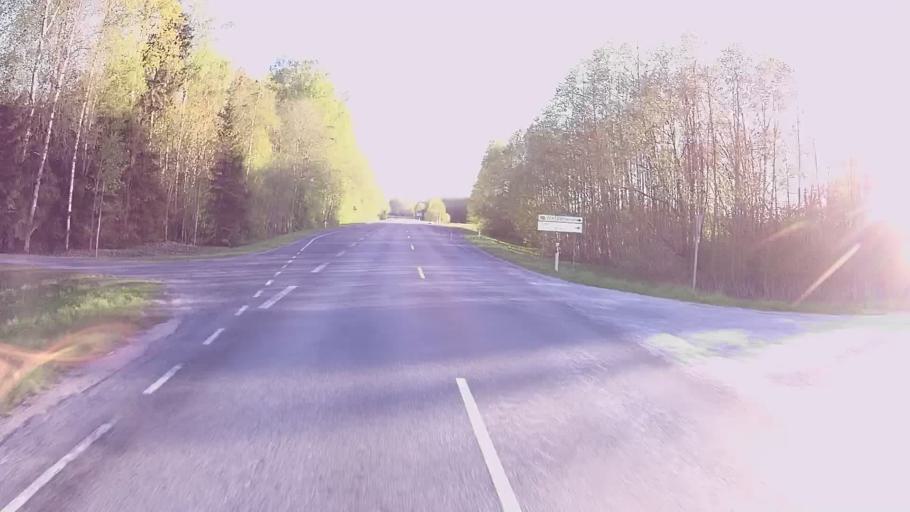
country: EE
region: Viljandimaa
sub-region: Viiratsi vald
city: Viiratsi
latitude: 58.4245
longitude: 25.7077
